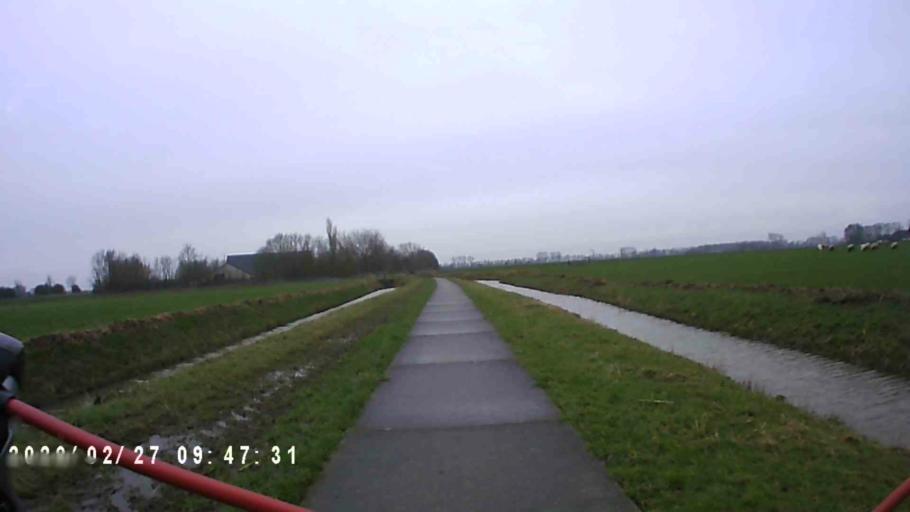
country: NL
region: Groningen
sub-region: Gemeente Zuidhorn
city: Aduard
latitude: 53.2737
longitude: 6.4488
